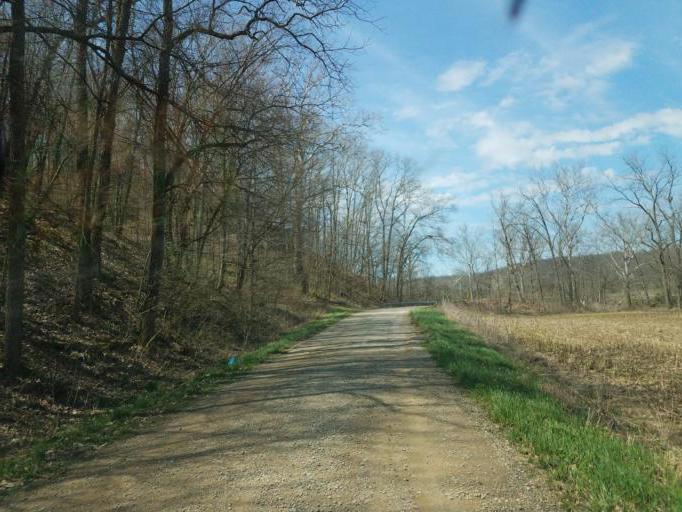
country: US
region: Ohio
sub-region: Knox County
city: Oak Hill
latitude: 40.3775
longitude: -82.2353
